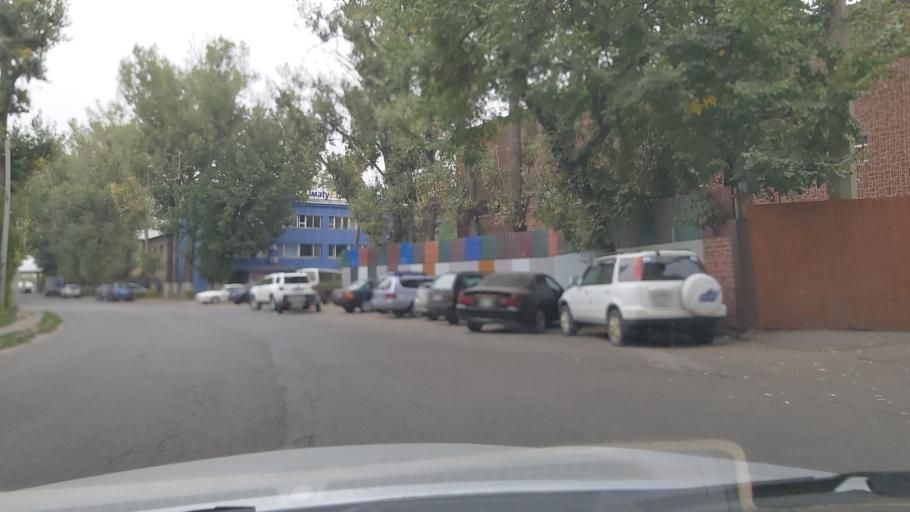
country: KZ
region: Almaty Oblysy
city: Pervomayskiy
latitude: 43.3532
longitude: 76.9798
